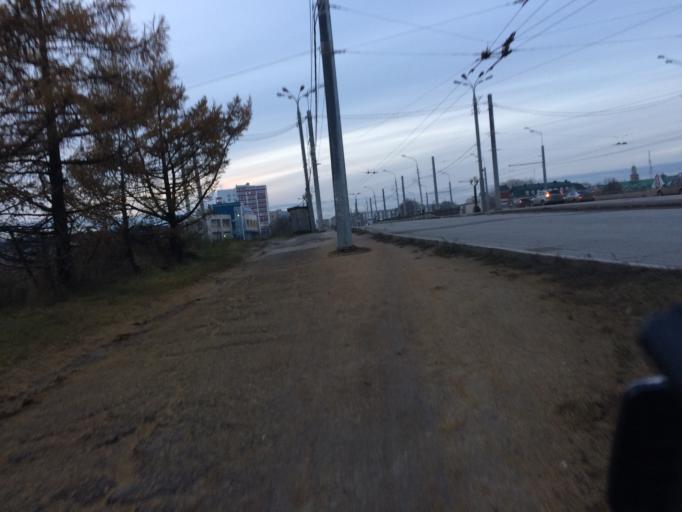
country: RU
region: Mariy-El
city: Yoshkar-Ola
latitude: 56.6279
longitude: 47.9011
